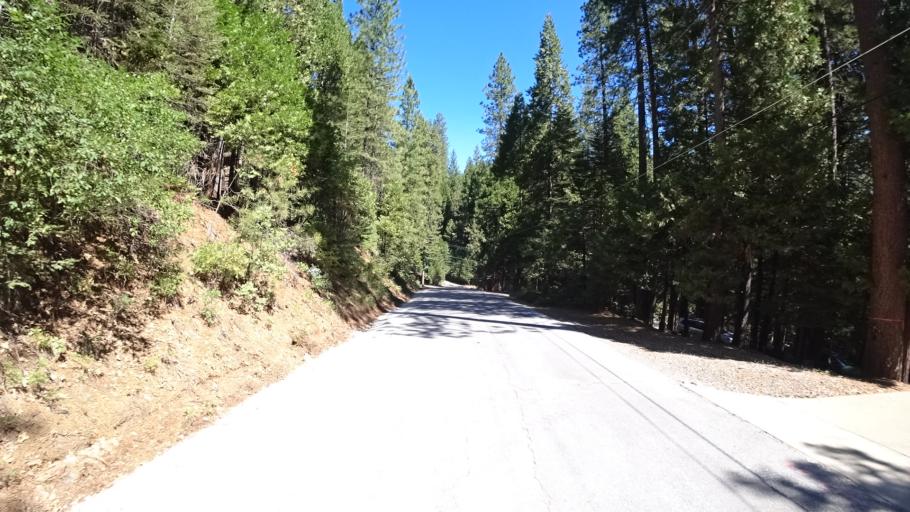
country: US
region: California
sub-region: Calaveras County
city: Arnold
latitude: 38.2524
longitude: -120.3392
